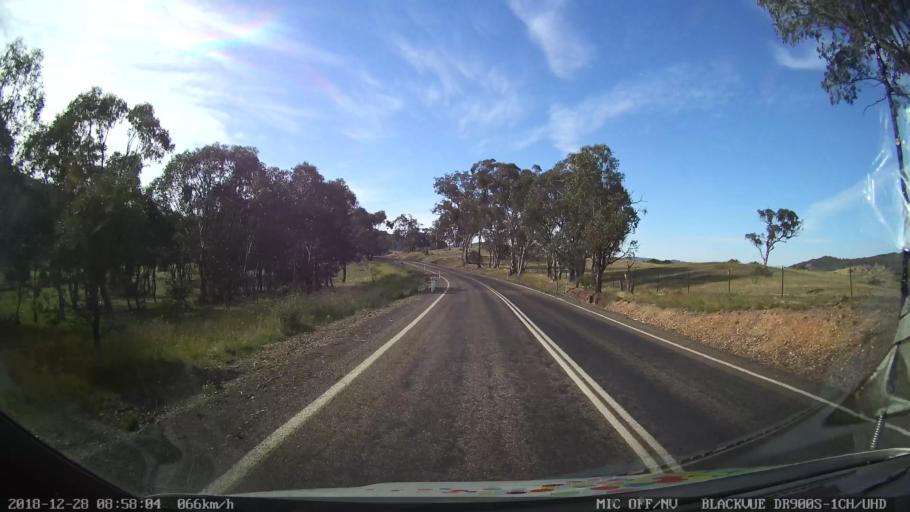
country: AU
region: New South Wales
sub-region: Upper Lachlan Shire
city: Crookwell
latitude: -34.1240
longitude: 149.3321
